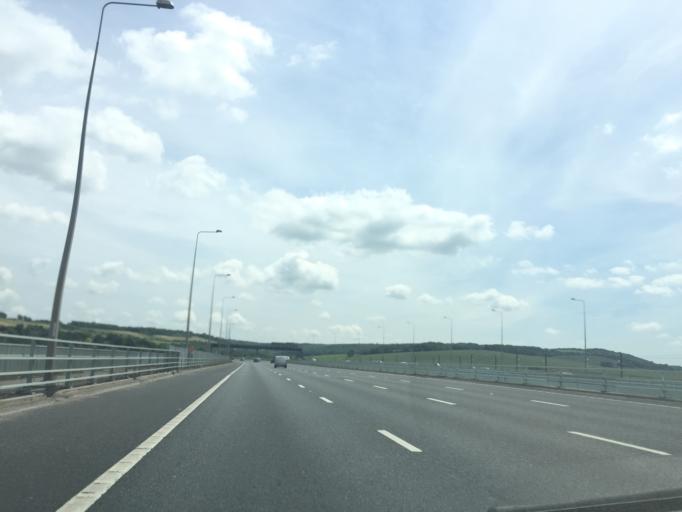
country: GB
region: England
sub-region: Medway
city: Cuxton
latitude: 51.3754
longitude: 0.4766
